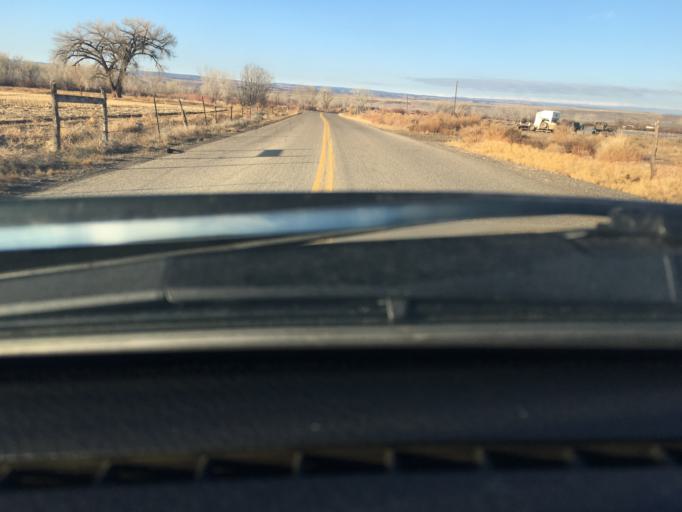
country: US
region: Colorado
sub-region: Delta County
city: Delta
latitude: 38.7481
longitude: -108.1389
